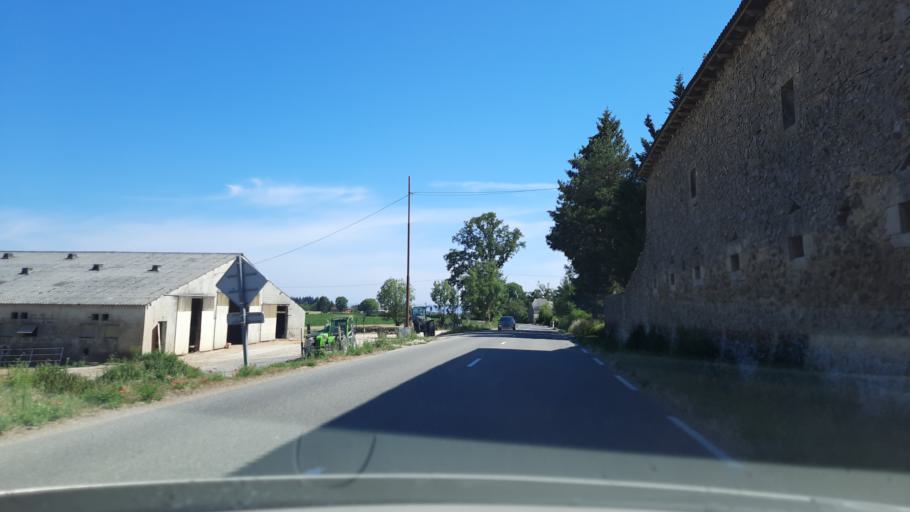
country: FR
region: Midi-Pyrenees
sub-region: Departement de l'Aveyron
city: Montbazens
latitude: 44.4349
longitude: 2.1946
